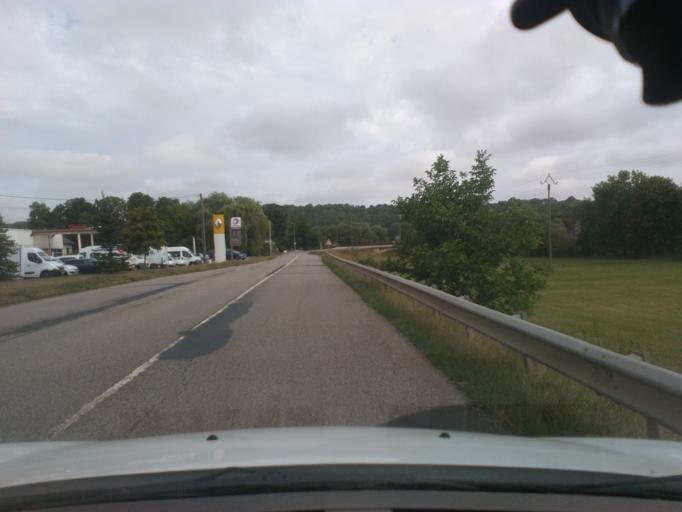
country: FR
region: Lorraine
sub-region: Departement de Meurthe-et-Moselle
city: Pulligny
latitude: 48.5223
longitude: 6.1581
